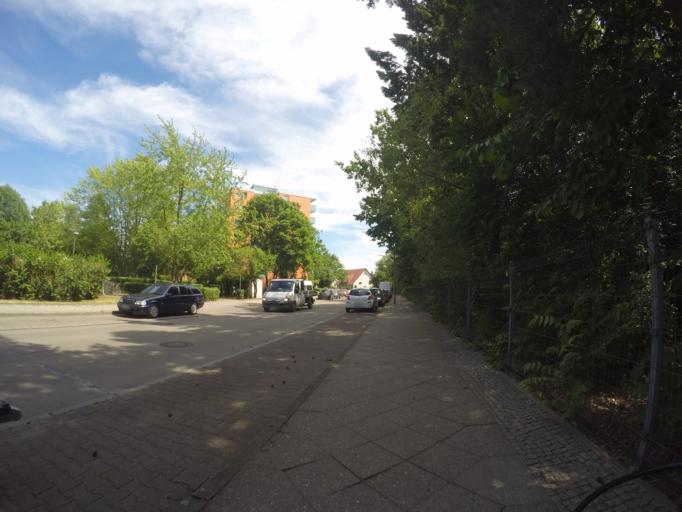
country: DE
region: Berlin
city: Mariendorf
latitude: 52.4386
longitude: 13.3975
